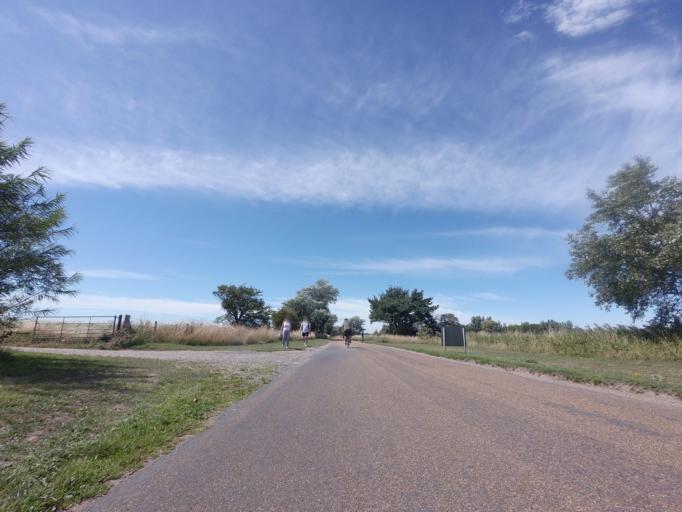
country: GB
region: England
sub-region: Kent
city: Sandwich
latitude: 51.2667
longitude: 1.3788
